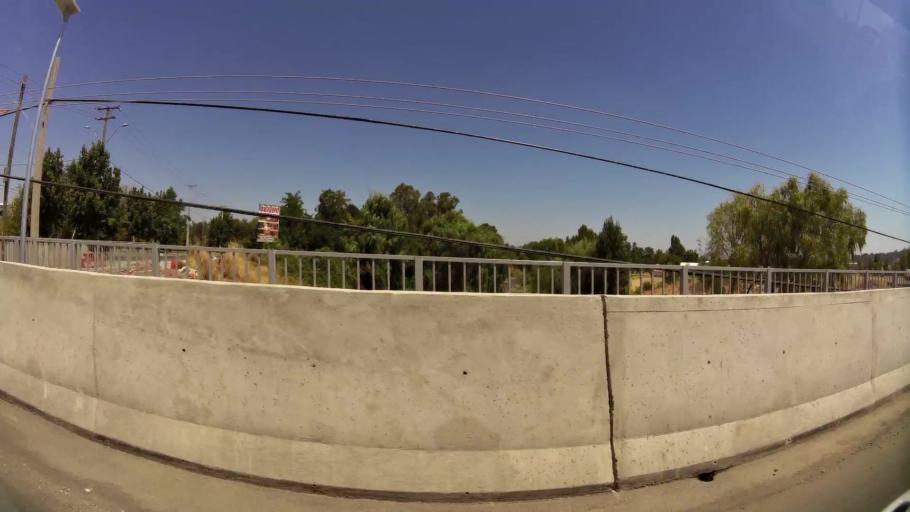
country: CL
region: Maule
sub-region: Provincia de Curico
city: Curico
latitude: -34.9903
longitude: -71.2099
